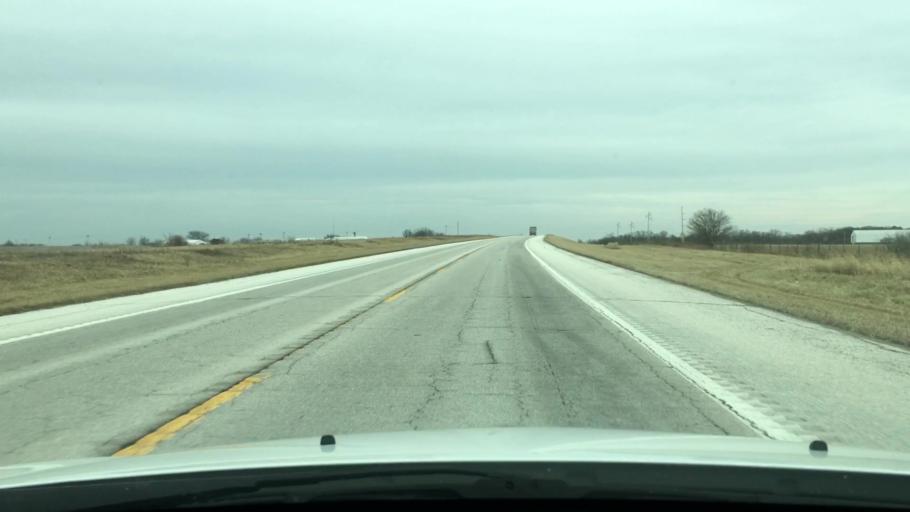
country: US
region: Missouri
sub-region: Pike County
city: Bowling Green
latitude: 39.3535
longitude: -91.2172
